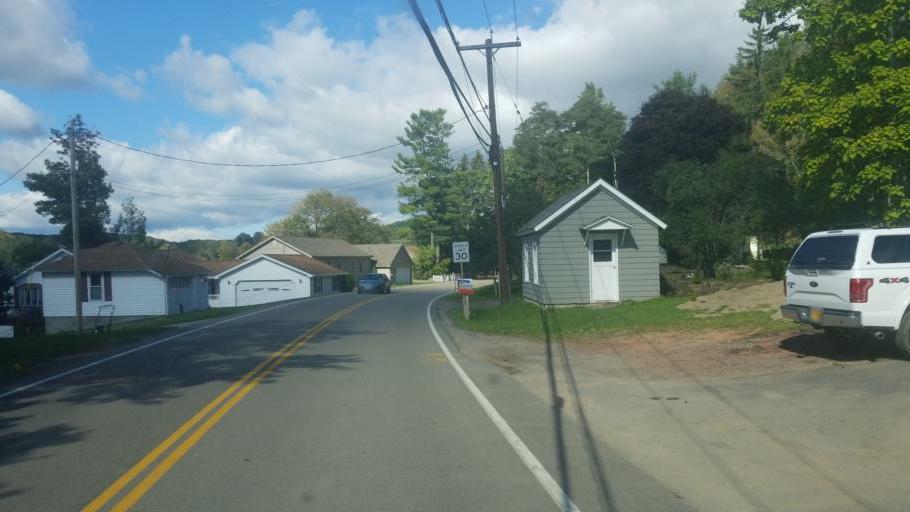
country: US
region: New York
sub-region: Allegany County
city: Cuba
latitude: 42.2554
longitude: -78.2903
